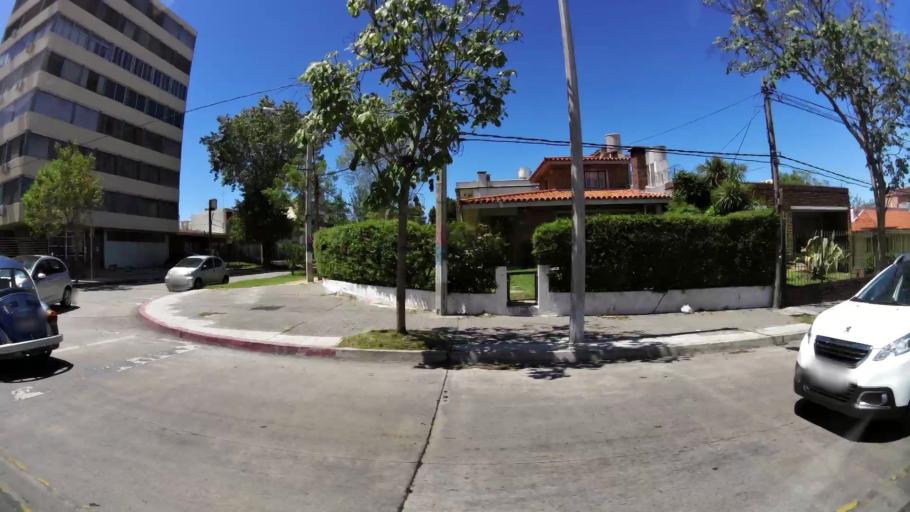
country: UY
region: Canelones
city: Paso de Carrasco
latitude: -34.8924
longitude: -56.1143
